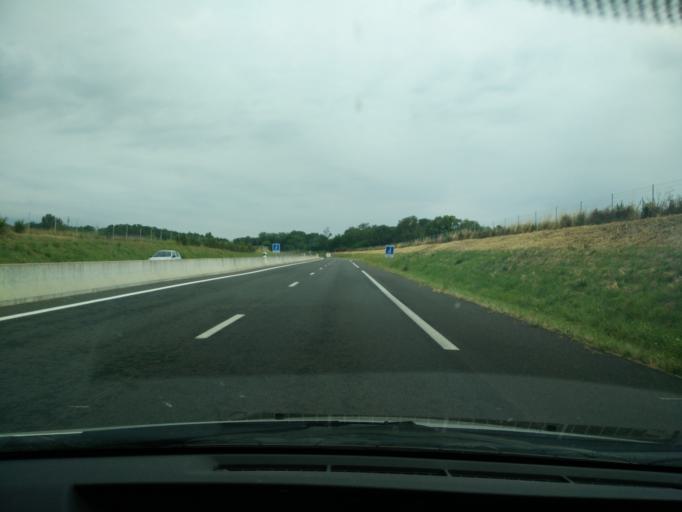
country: FR
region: Pays de la Loire
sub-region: Departement de Maine-et-Loire
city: Saint-Jean
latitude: 47.2988
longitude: -0.3895
